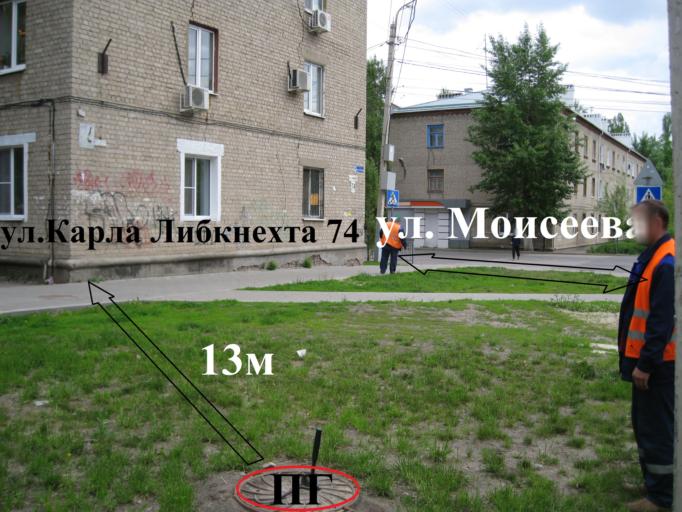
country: RU
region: Voronezj
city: Voronezh
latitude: 51.6486
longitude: 39.1716
